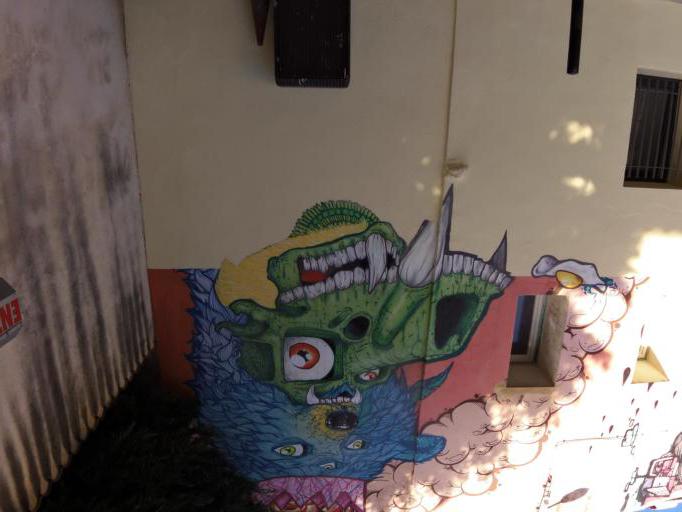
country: FR
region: Languedoc-Roussillon
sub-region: Departement du Gard
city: Nimes
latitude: 43.8401
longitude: 4.3662
